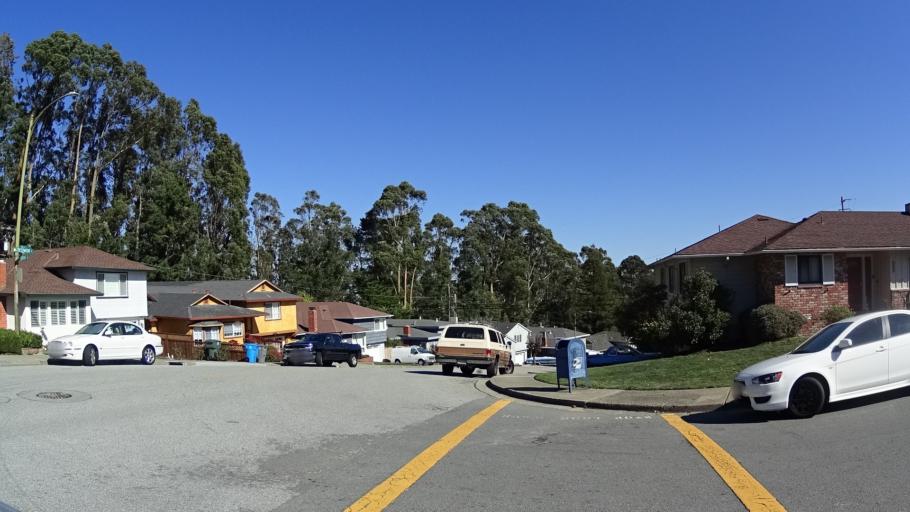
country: US
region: California
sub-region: San Mateo County
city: San Bruno
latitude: 37.6250
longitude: -122.4321
